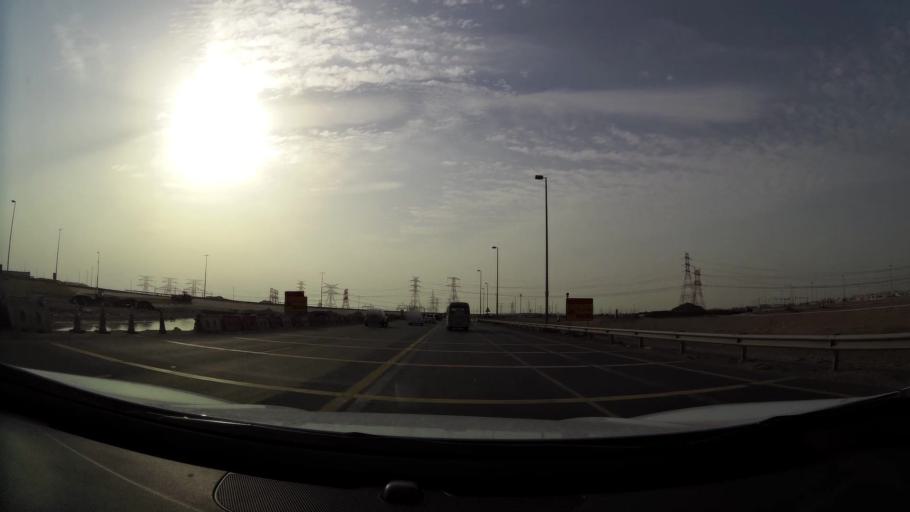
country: AE
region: Abu Dhabi
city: Abu Dhabi
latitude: 24.2941
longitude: 54.5494
